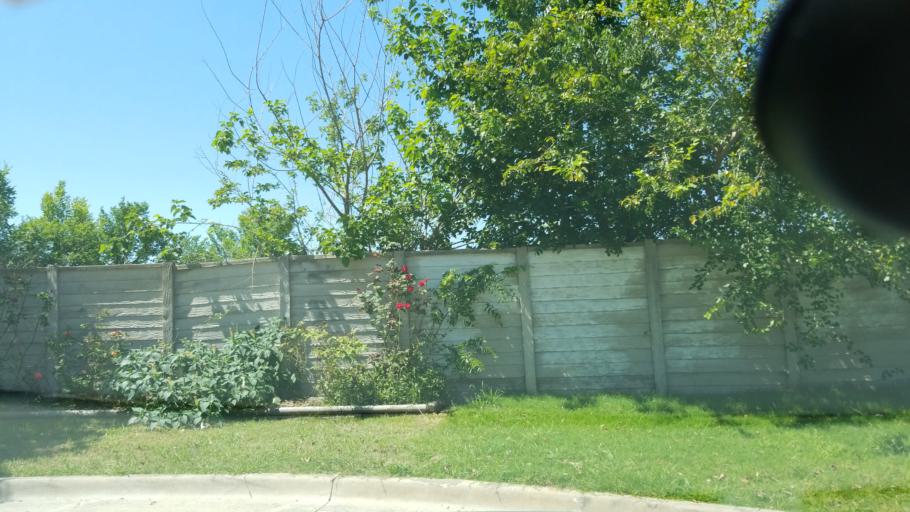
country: US
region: Texas
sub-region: Dallas County
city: Irving
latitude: 32.8331
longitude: -96.9396
